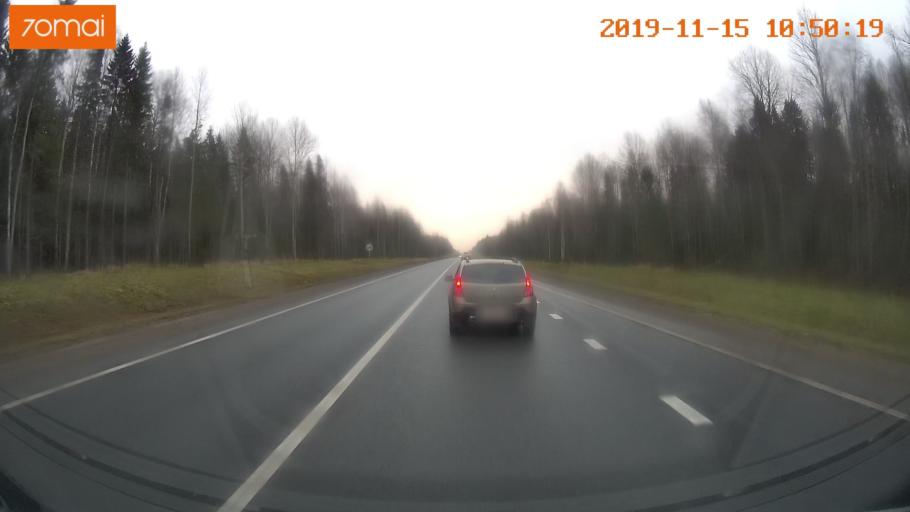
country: RU
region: Vologda
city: Chebsara
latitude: 59.1858
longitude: 38.6791
